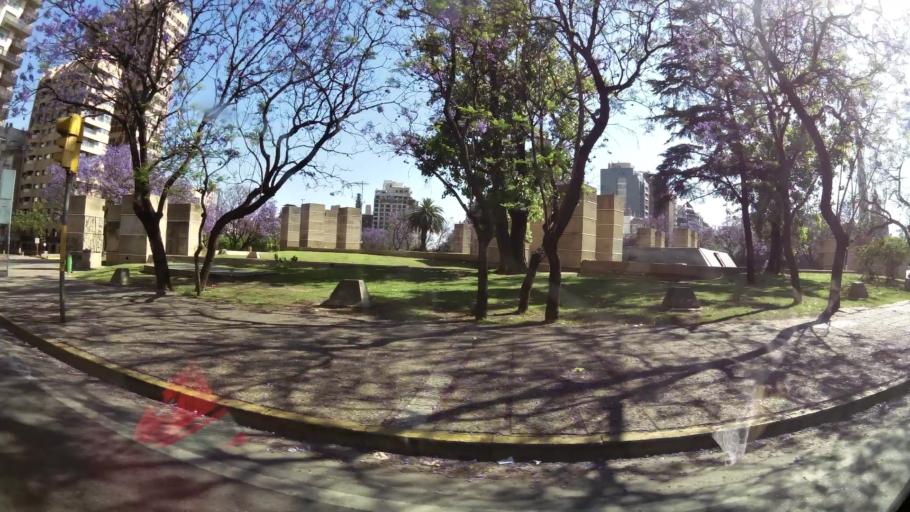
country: AR
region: Cordoba
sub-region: Departamento de Capital
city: Cordoba
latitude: -31.4290
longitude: -64.1851
